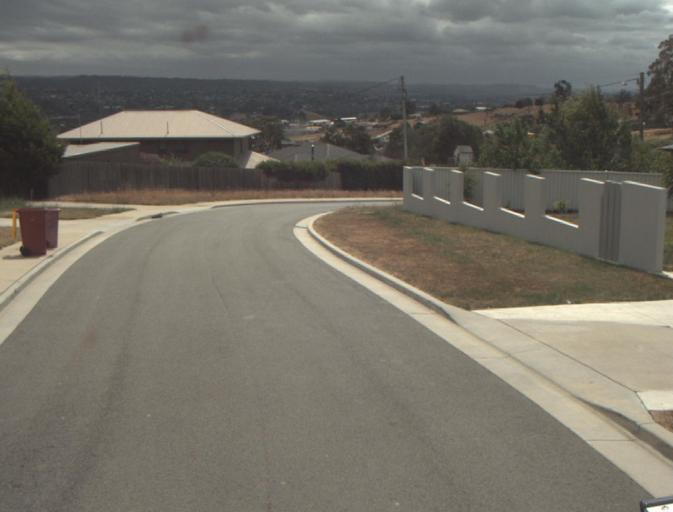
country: AU
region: Tasmania
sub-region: Launceston
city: Newstead
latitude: -41.4547
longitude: 147.2032
